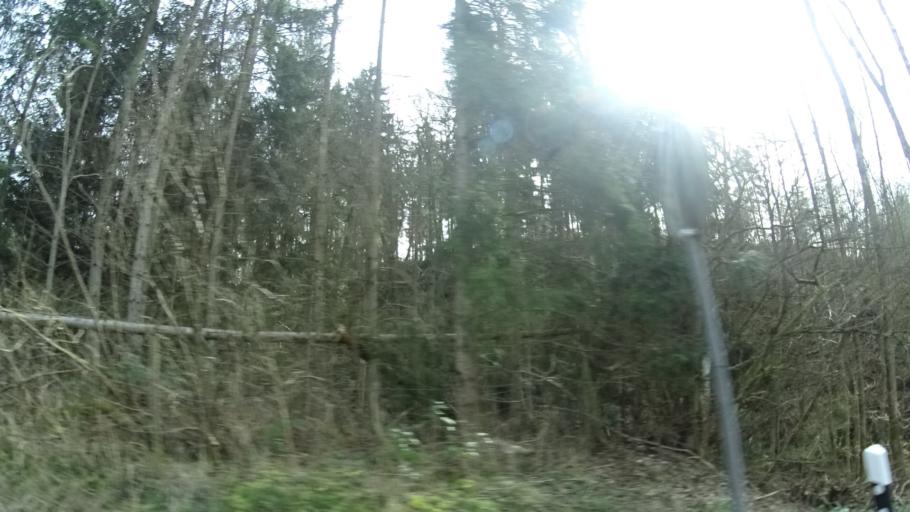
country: DE
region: Rheinland-Pfalz
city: Munchwald
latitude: 49.9134
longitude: 7.6670
